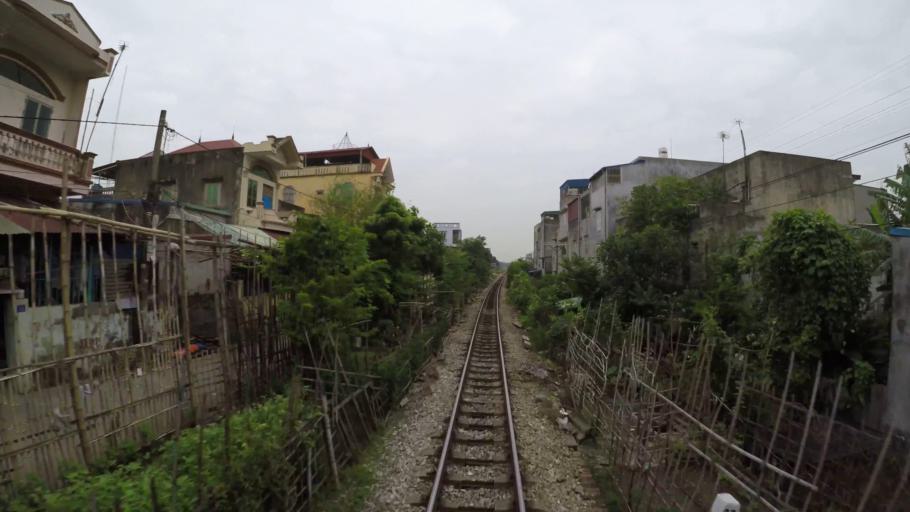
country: VN
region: Hai Phong
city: An Duong
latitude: 20.8856
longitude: 106.6021
